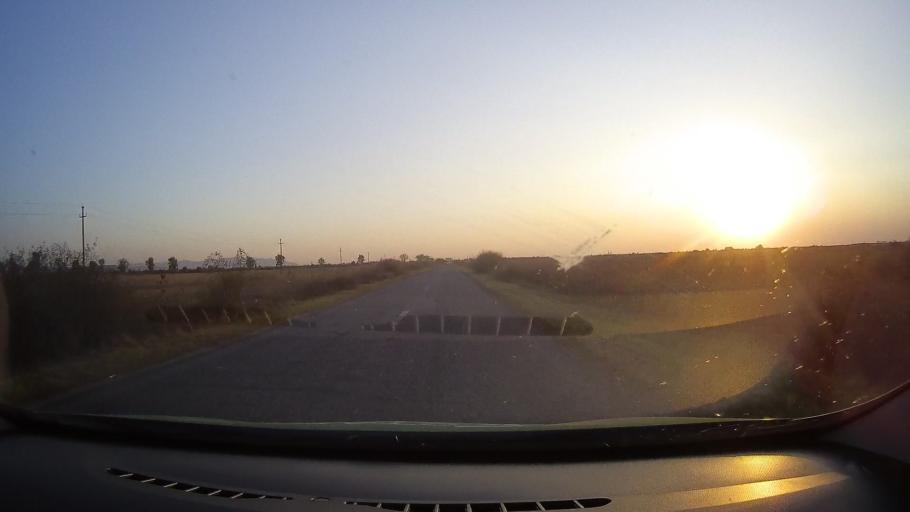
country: RO
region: Arad
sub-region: Comuna Seleus
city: Seleus
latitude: 46.3972
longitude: 21.7196
